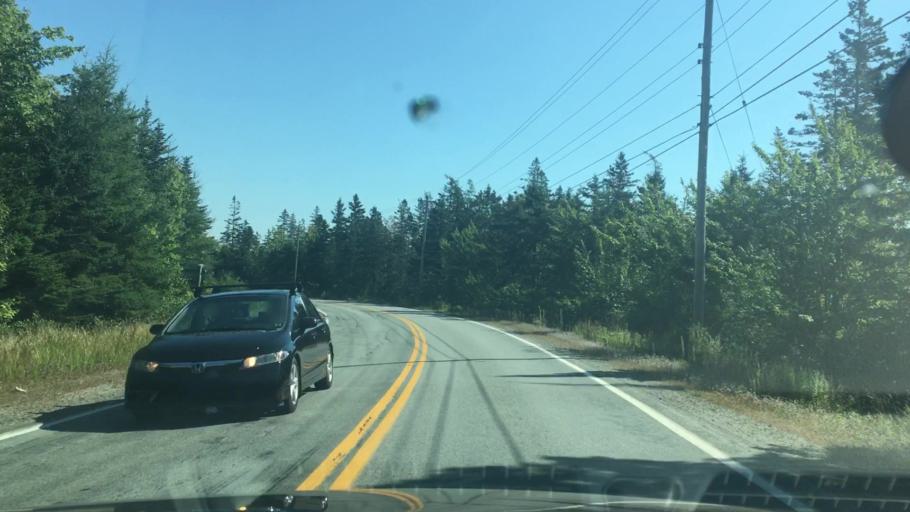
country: CA
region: Nova Scotia
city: New Glasgow
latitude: 44.9104
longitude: -62.5446
